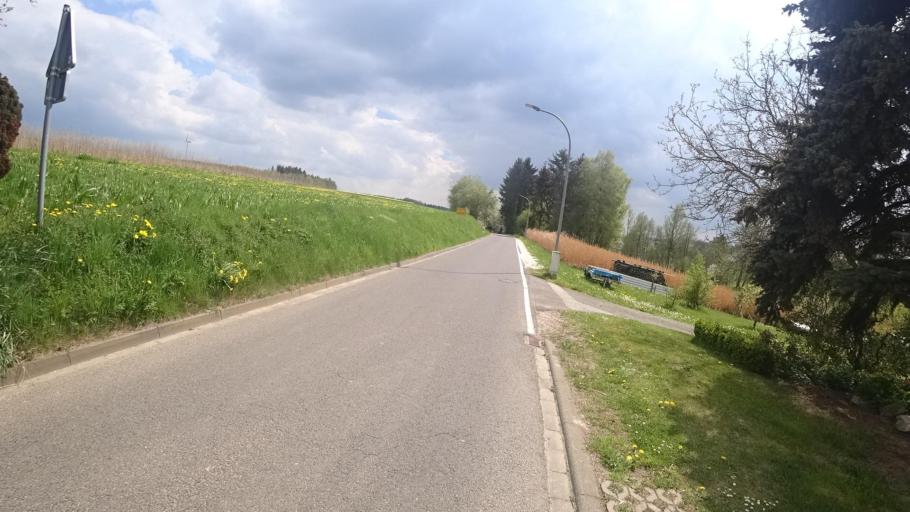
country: DE
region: Rheinland-Pfalz
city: Klosterkumbd
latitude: 50.0262
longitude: 7.5367
